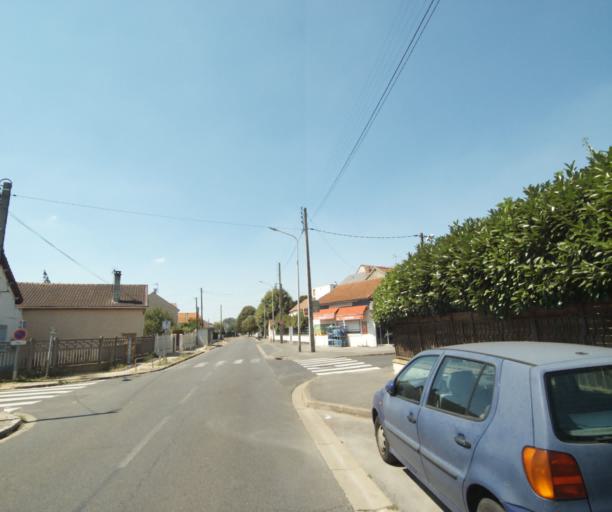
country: FR
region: Ile-de-France
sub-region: Departement de Seine-et-Marne
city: Lagny-sur-Marne
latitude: 48.8651
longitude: 2.7170
